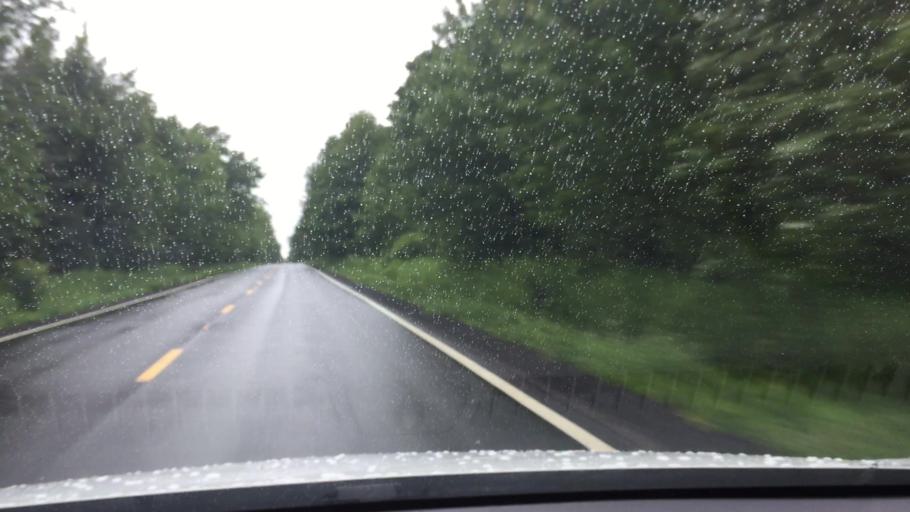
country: US
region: Massachusetts
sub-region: Berkshire County
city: Hinsdale
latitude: 42.3744
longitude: -73.1486
